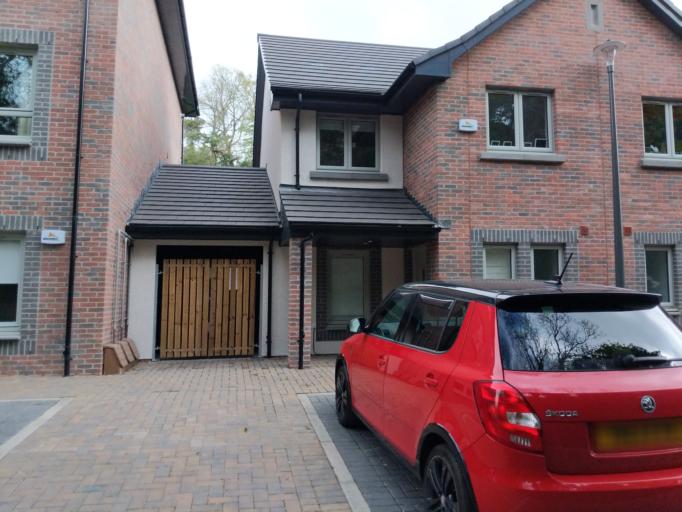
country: GB
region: Scotland
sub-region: Edinburgh
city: Currie
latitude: 55.8992
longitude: -3.2958
